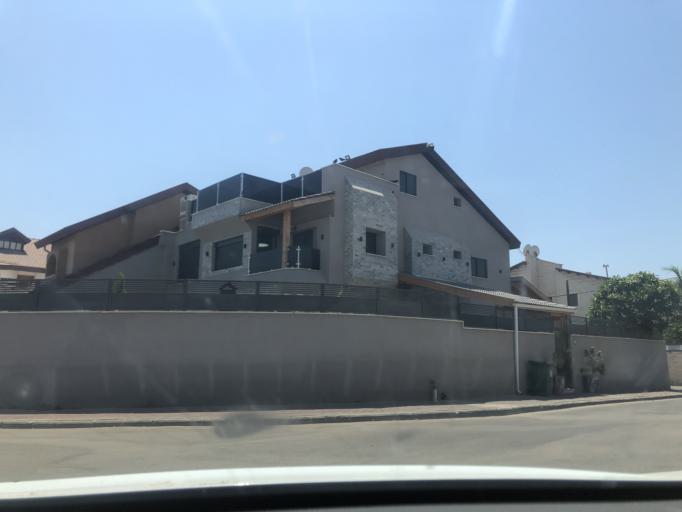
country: IL
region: Central District
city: Lod
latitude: 31.9374
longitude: 34.8890
